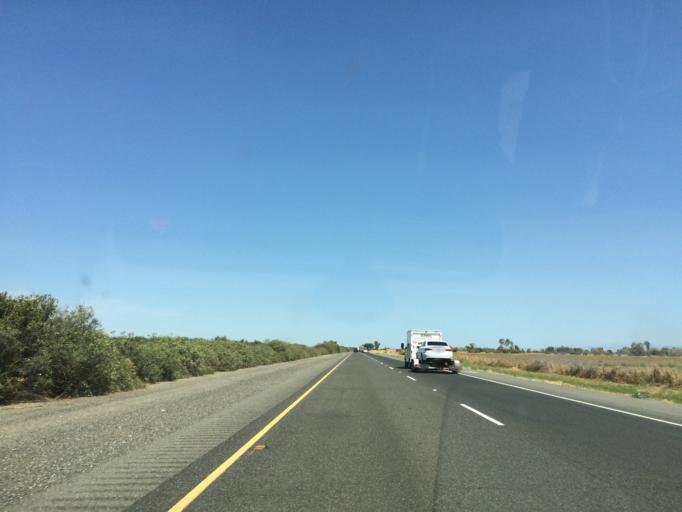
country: US
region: California
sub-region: Glenn County
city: Willows
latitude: 39.6126
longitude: -122.2070
